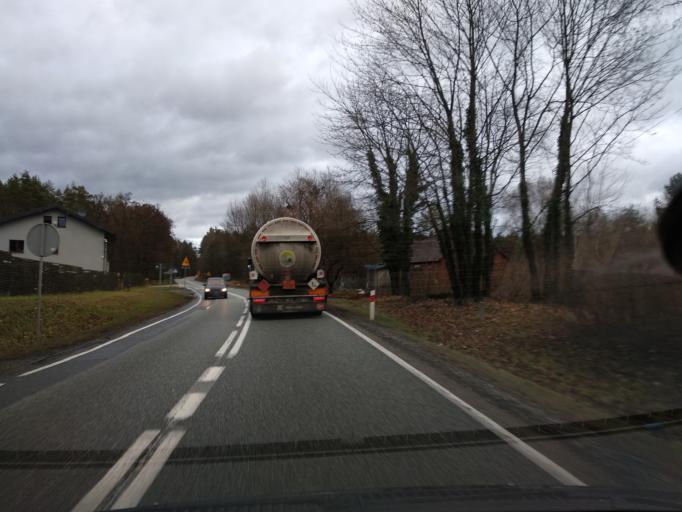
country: PL
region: Lower Silesian Voivodeship
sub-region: Powiat olesnicki
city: Twardogora
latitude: 51.3006
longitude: 17.5357
